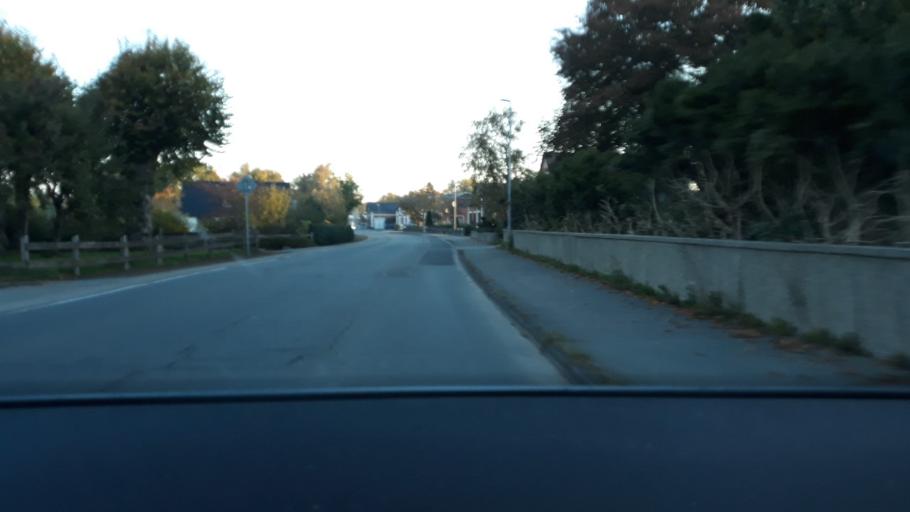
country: DE
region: Schleswig-Holstein
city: Satrup
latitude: 54.6796
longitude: 9.6029
